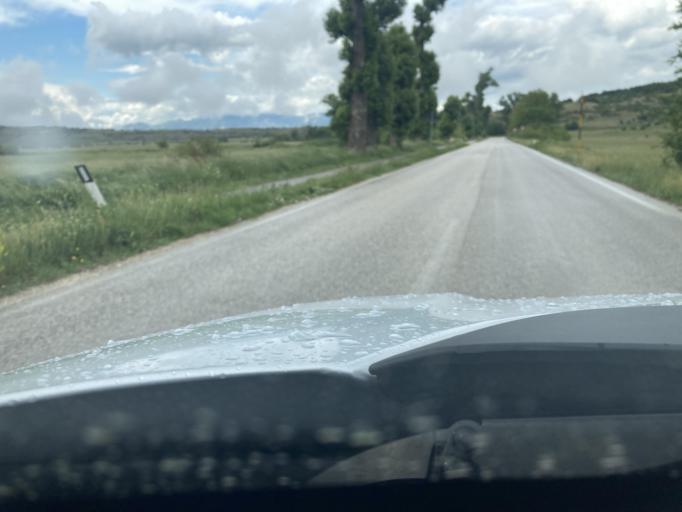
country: IT
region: Abruzzo
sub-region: Provincia dell' Aquila
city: Rocca di Mezzo
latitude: 42.2185
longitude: 13.5313
